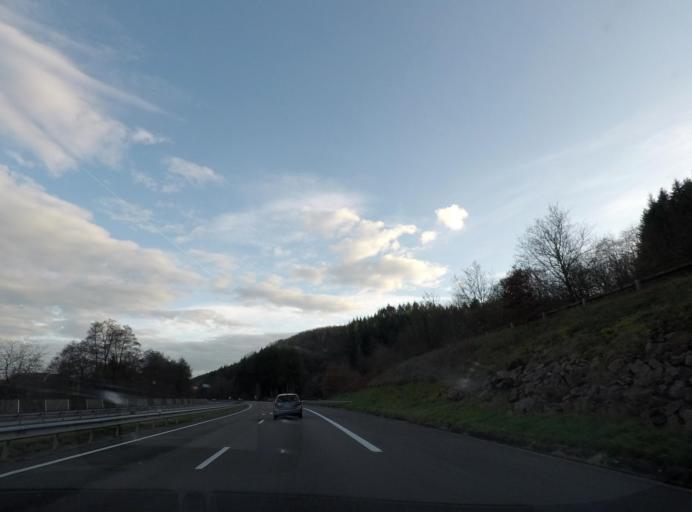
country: FR
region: Bourgogne
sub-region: Departement de Saone-et-Loire
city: Matour
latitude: 46.3774
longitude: 4.5298
